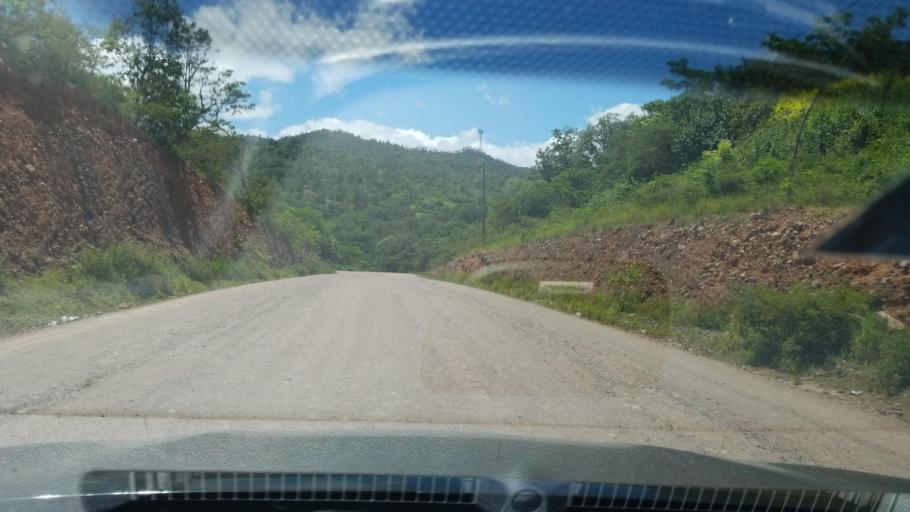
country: HN
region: Francisco Morazan
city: San Juan de Flores
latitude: 14.3369
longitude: -87.0456
